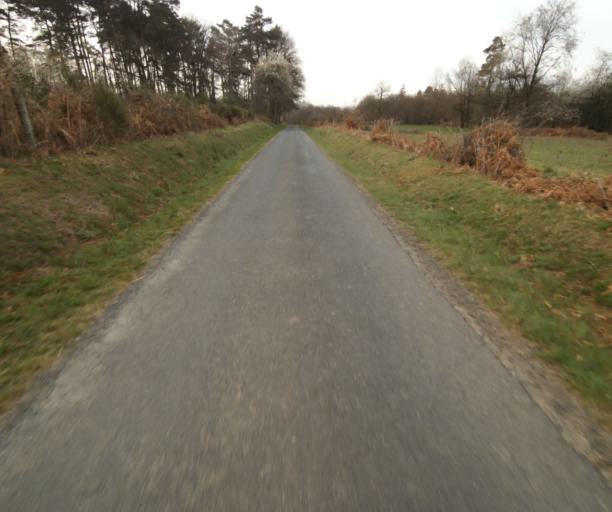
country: FR
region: Limousin
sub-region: Departement de la Correze
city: Correze
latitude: 45.4438
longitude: 1.8210
